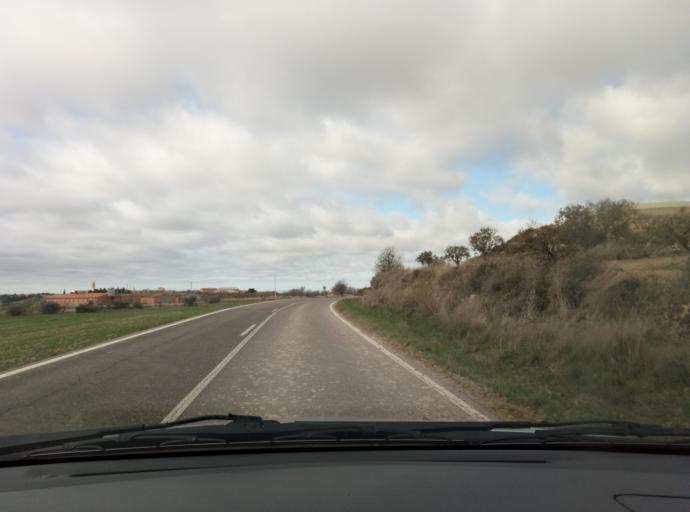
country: ES
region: Catalonia
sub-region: Provincia de Lleida
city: Vallbona de les Monges
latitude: 41.5619
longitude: 1.0733
